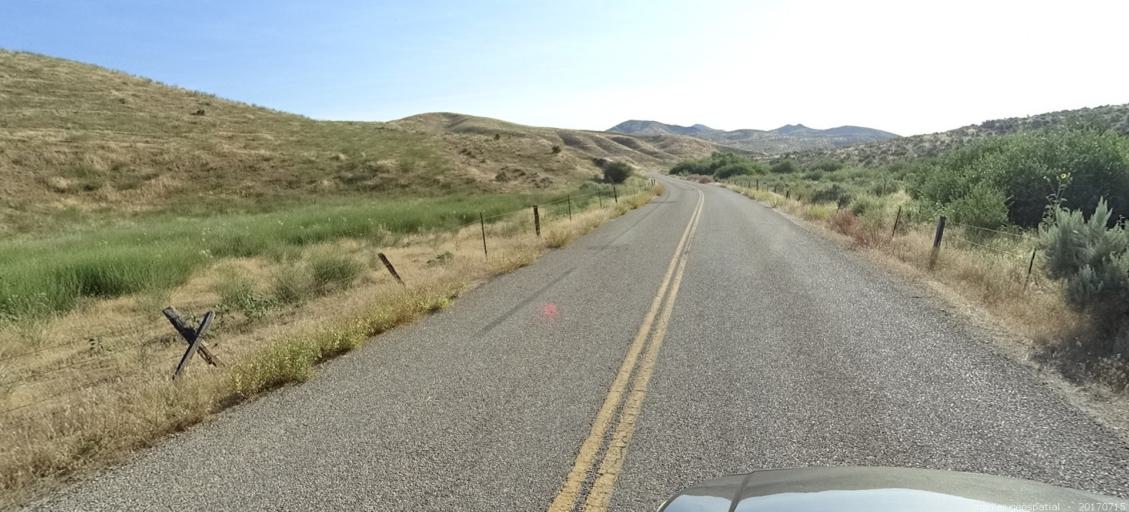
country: US
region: Idaho
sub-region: Ada County
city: Boise
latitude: 43.4805
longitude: -115.9799
